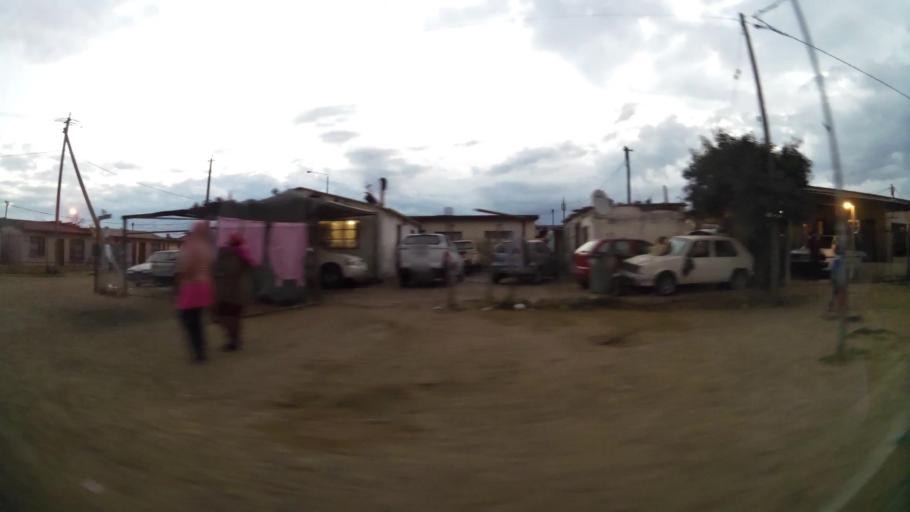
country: ZA
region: Orange Free State
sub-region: Lejweleputswa District Municipality
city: Welkom
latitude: -27.9601
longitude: 26.7855
